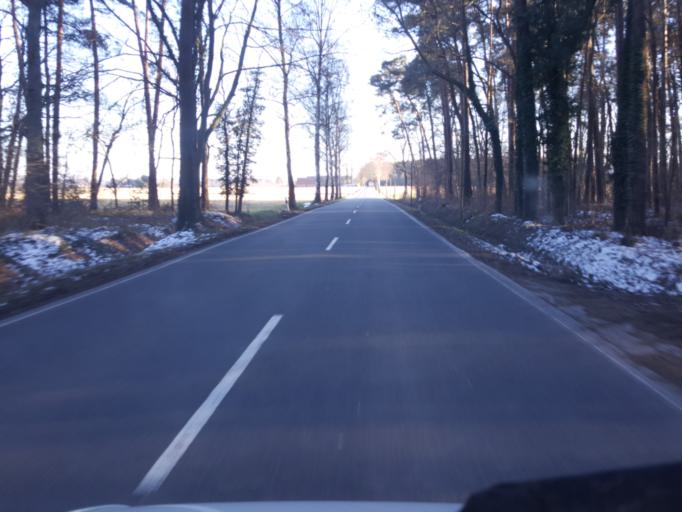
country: DE
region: North Rhine-Westphalia
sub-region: Regierungsbezirk Detmold
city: Hille
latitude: 52.3813
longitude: 8.7257
